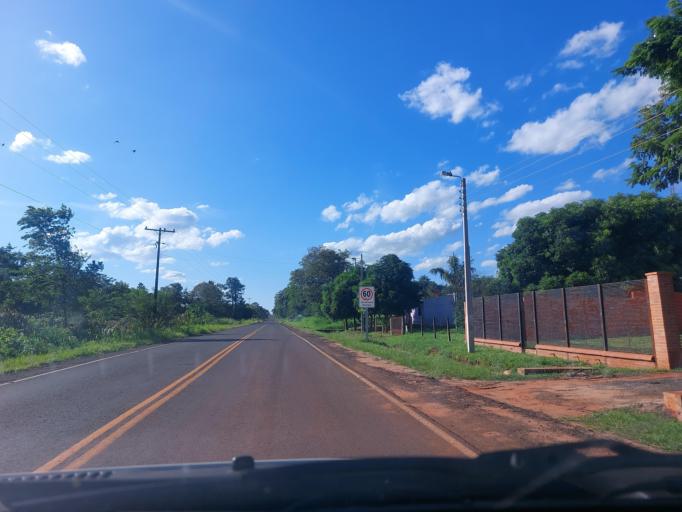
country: PY
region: San Pedro
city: Guayaybi
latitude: -24.5924
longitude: -56.5196
